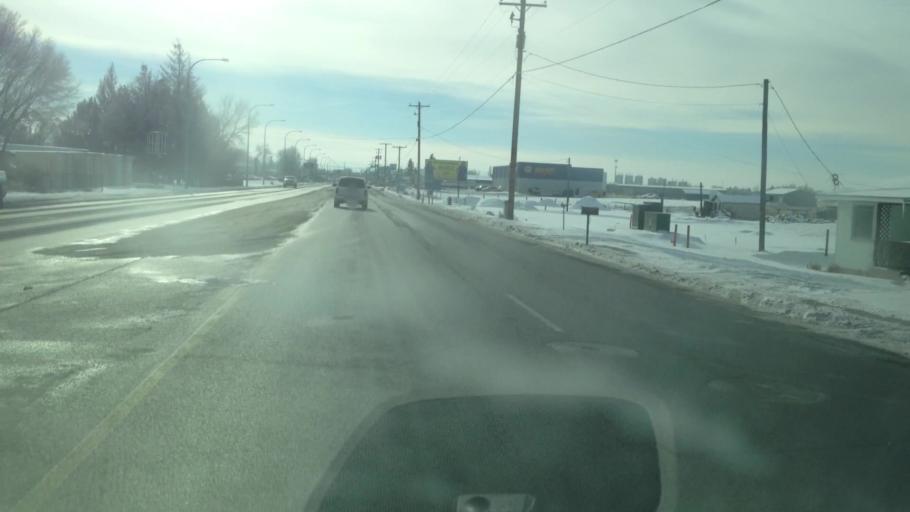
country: US
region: Idaho
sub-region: Bonneville County
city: Idaho Falls
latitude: 43.5201
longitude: -112.0236
